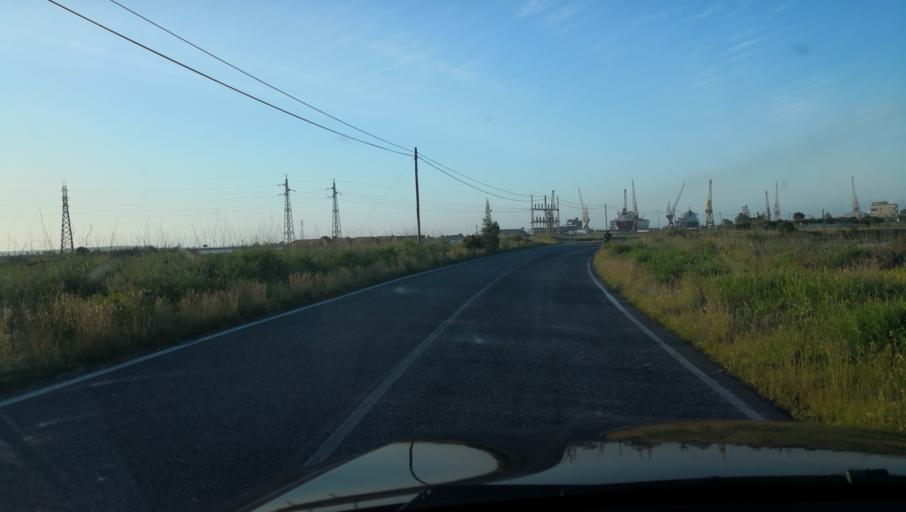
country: PT
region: Setubal
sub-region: Setubal
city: Setubal
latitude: 38.4887
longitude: -8.7935
